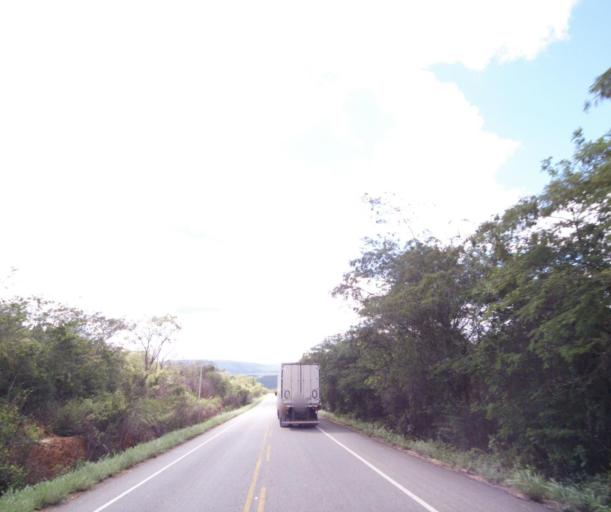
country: BR
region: Bahia
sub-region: Caetite
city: Caetite
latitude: -14.1325
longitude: -42.3900
